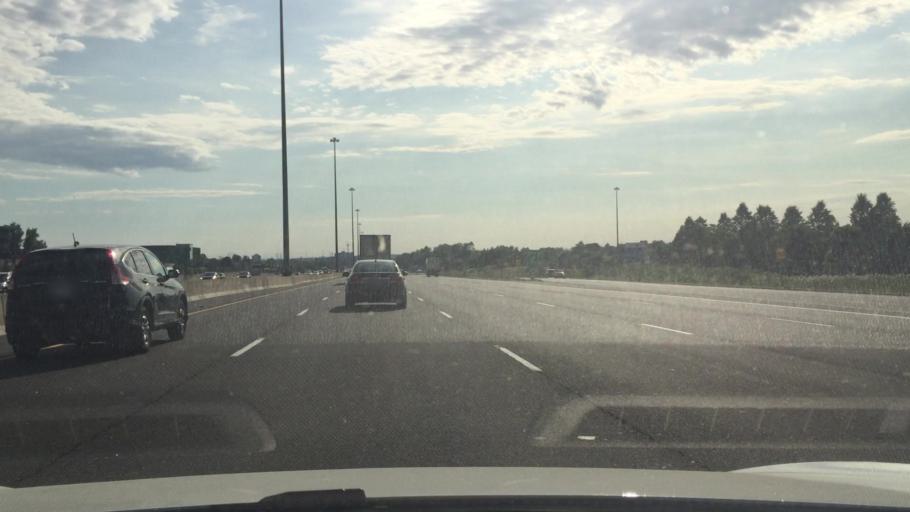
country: CA
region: Ontario
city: Ajax
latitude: 43.8509
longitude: -79.0354
